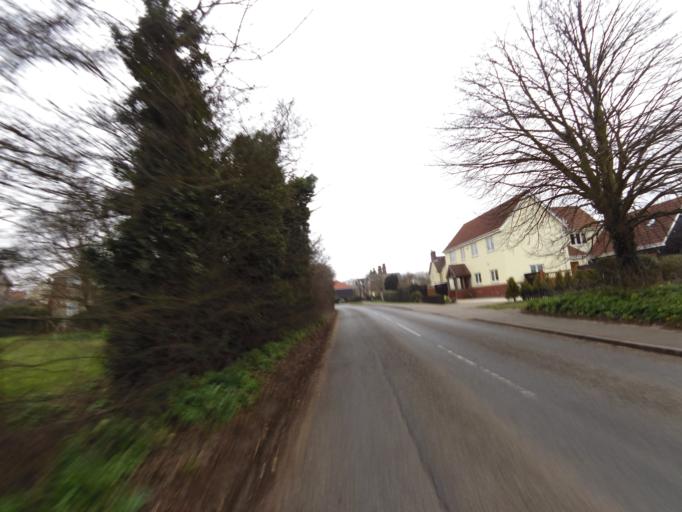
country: GB
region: England
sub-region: Suffolk
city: Wickham Market
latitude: 52.1512
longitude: 1.3967
